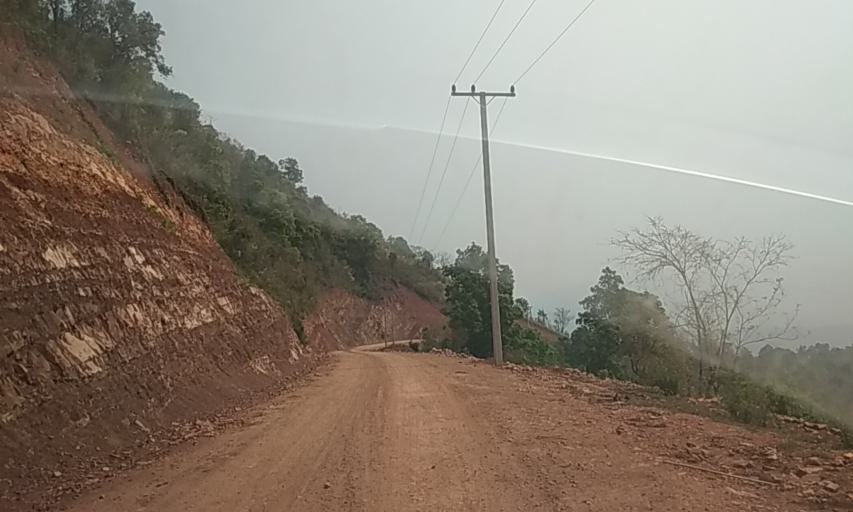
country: VN
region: Huyen Dien Bien
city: Dien Bien Phu
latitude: 21.4987
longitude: 102.7885
